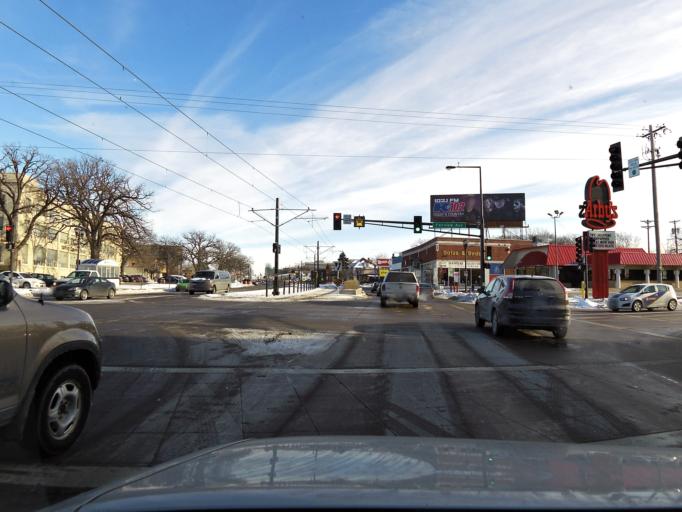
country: US
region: Minnesota
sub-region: Ramsey County
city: Falcon Heights
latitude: 44.9558
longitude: -93.1773
